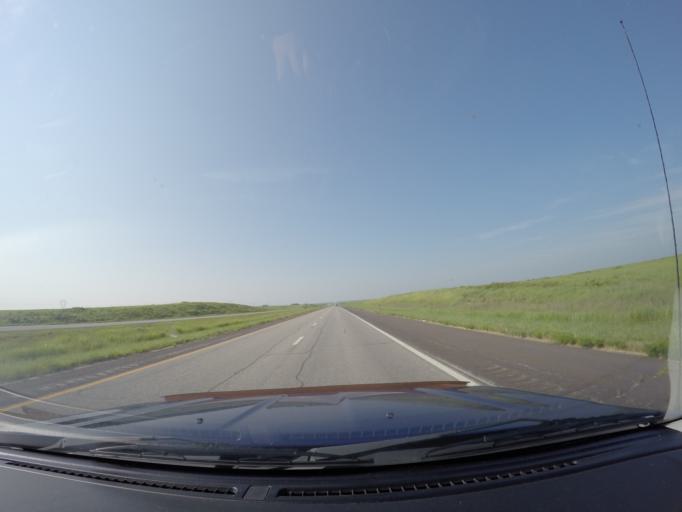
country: US
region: Kansas
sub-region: Riley County
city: Manhattan
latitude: 39.1194
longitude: -96.5384
